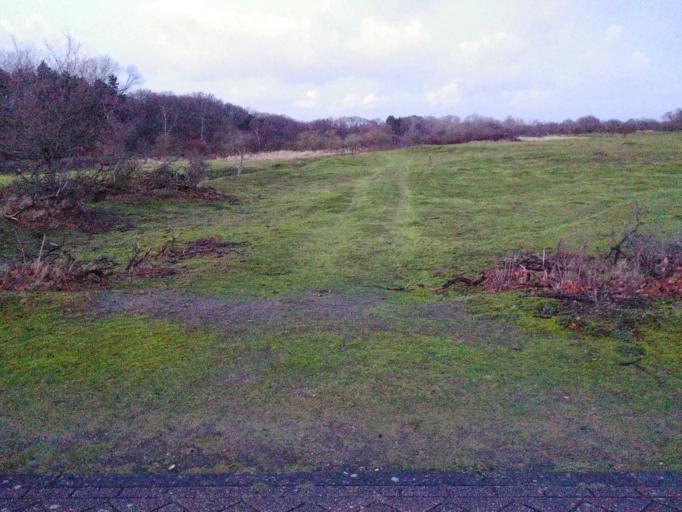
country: NL
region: South Holland
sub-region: Gemeente Lisse
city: Lisse
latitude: 52.3039
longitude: 4.5270
